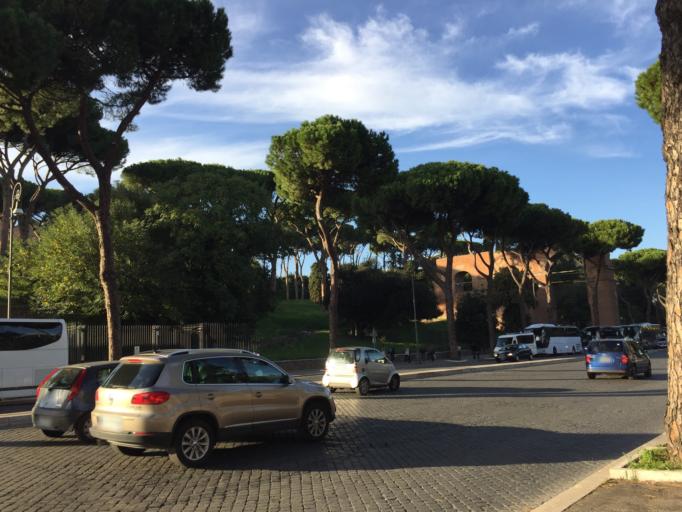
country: IT
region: Latium
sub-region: Citta metropolitana di Roma Capitale
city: Rome
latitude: 41.8861
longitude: 12.4898
